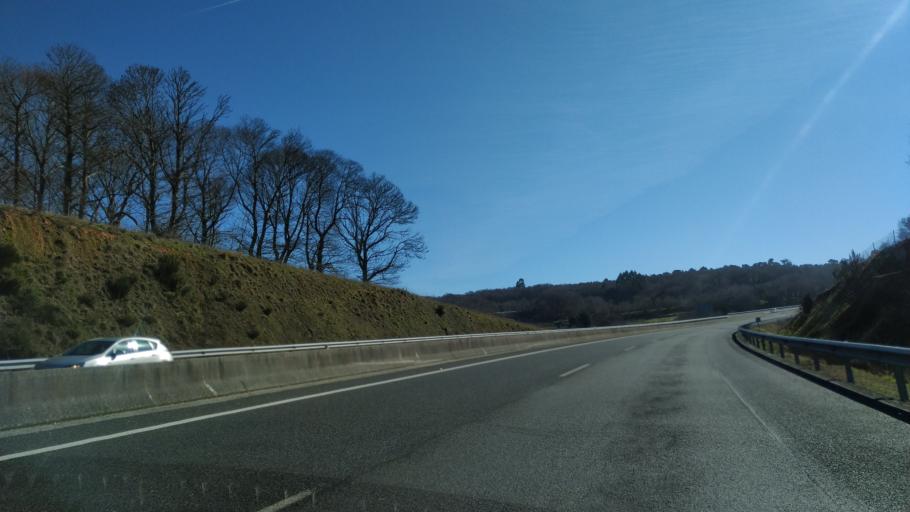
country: ES
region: Galicia
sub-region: Provincia de Pontevedra
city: Lalin
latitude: 42.6313
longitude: -8.1221
